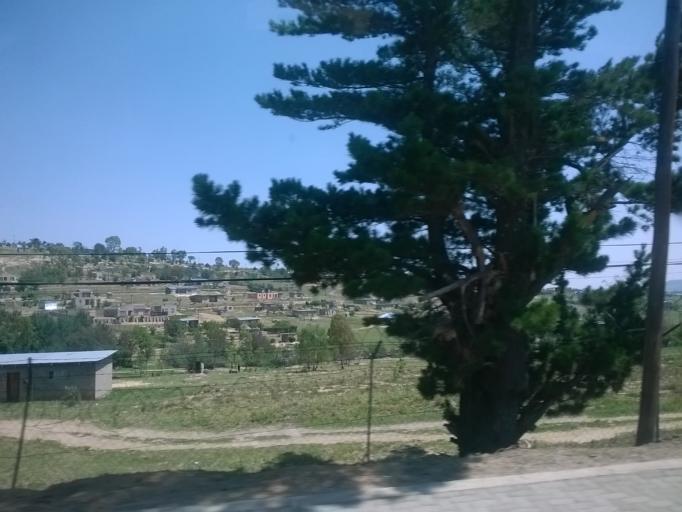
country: LS
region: Berea
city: Teyateyaneng
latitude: -29.1405
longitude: 27.7639
